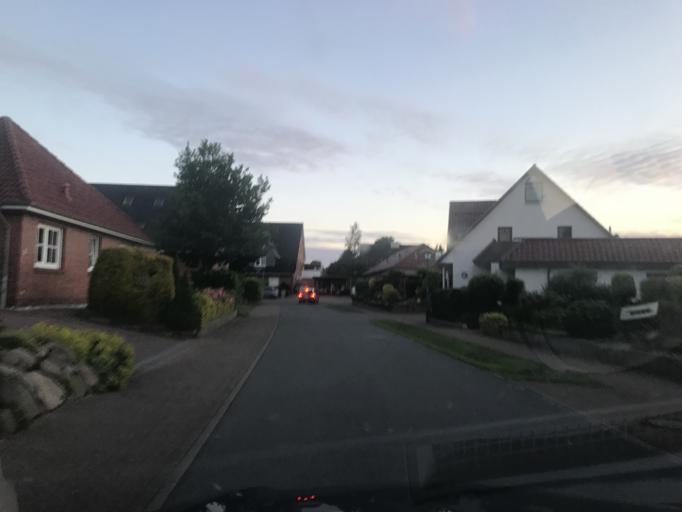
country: DE
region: Schleswig-Holstein
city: Burg
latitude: 54.0019
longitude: 9.2628
